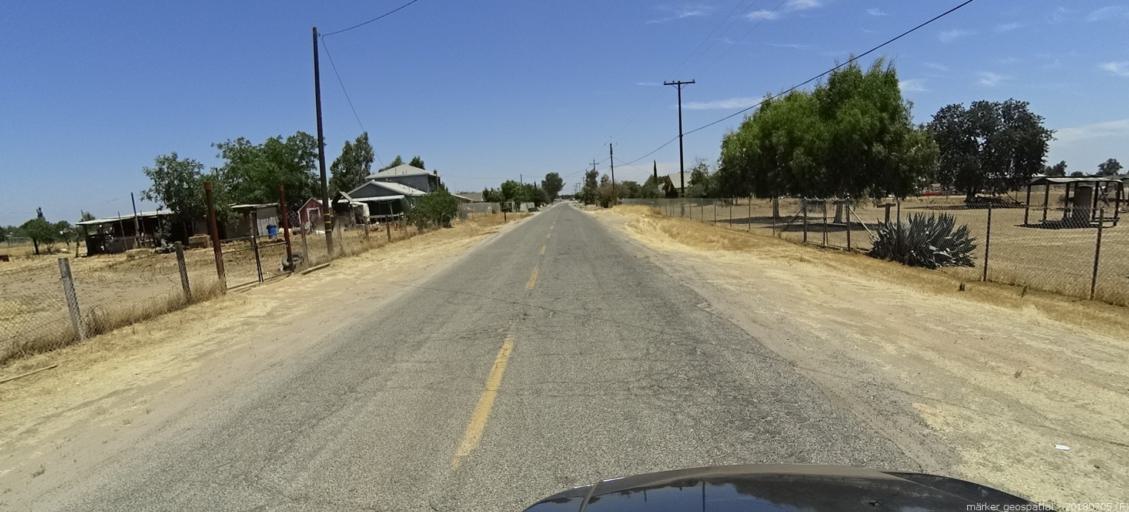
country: US
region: California
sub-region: Madera County
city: Madera
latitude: 36.9940
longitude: -120.0280
